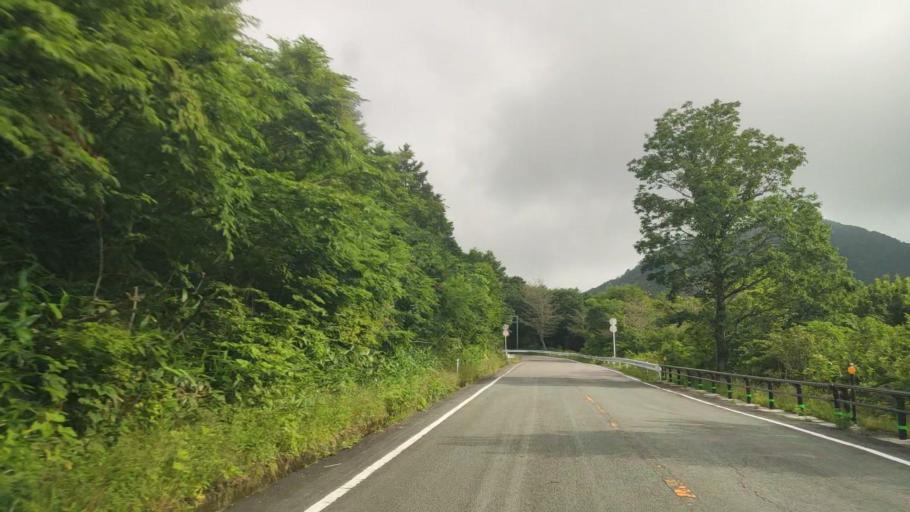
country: JP
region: Tottori
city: Kurayoshi
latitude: 35.3314
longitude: 133.5927
